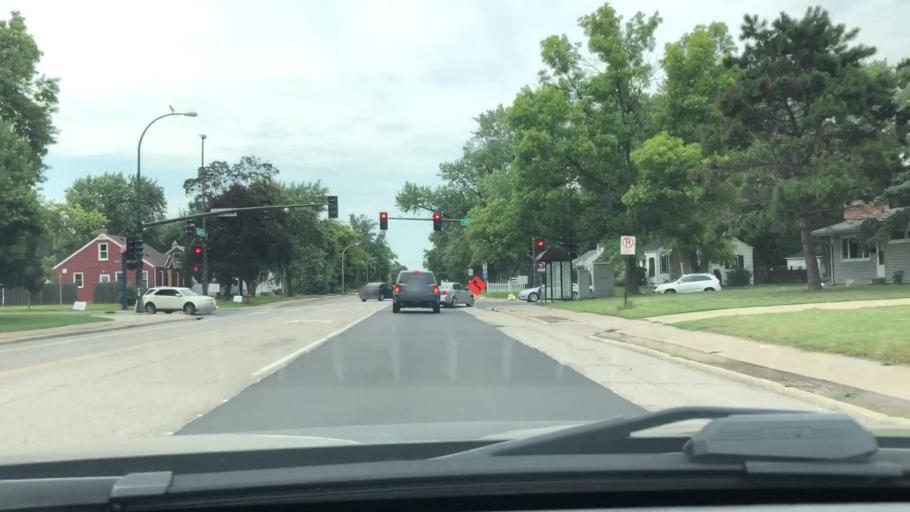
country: US
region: Minnesota
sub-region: Hennepin County
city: Richfield
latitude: 44.8650
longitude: -93.2782
